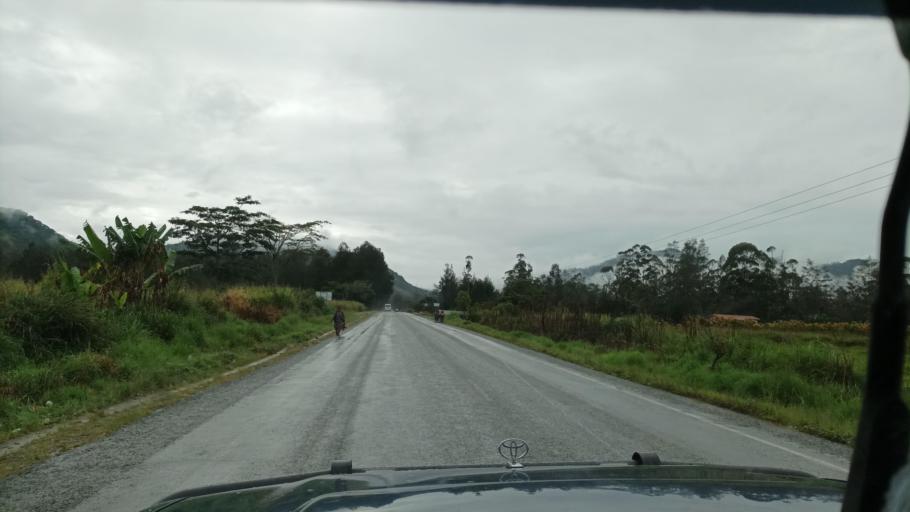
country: PG
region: Western Highlands
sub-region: Hagen
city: Mount Hagen
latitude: -5.8366
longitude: 144.3331
